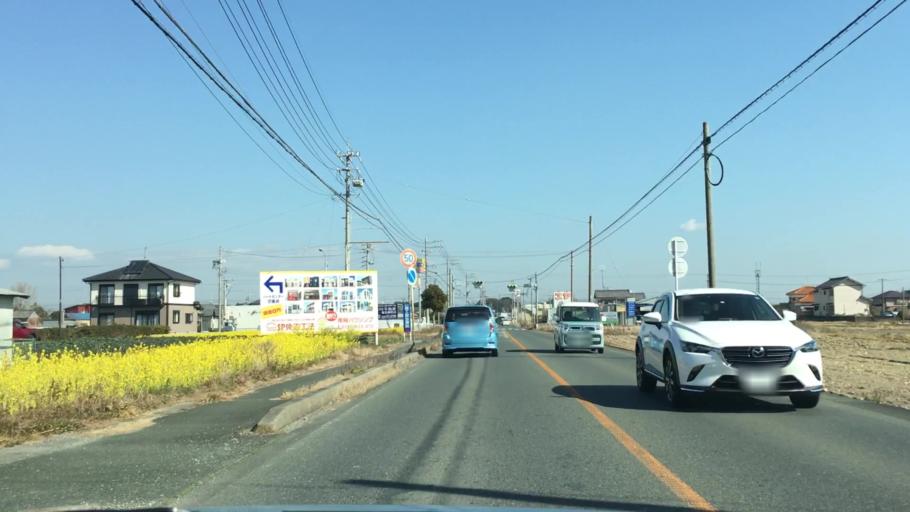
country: JP
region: Aichi
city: Tahara
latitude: 34.6877
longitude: 137.3223
